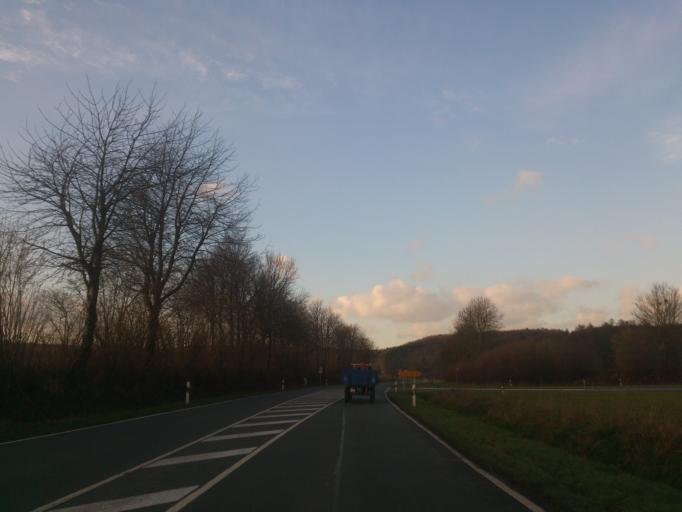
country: DE
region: North Rhine-Westphalia
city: Brakel
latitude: 51.7328
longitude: 9.1641
